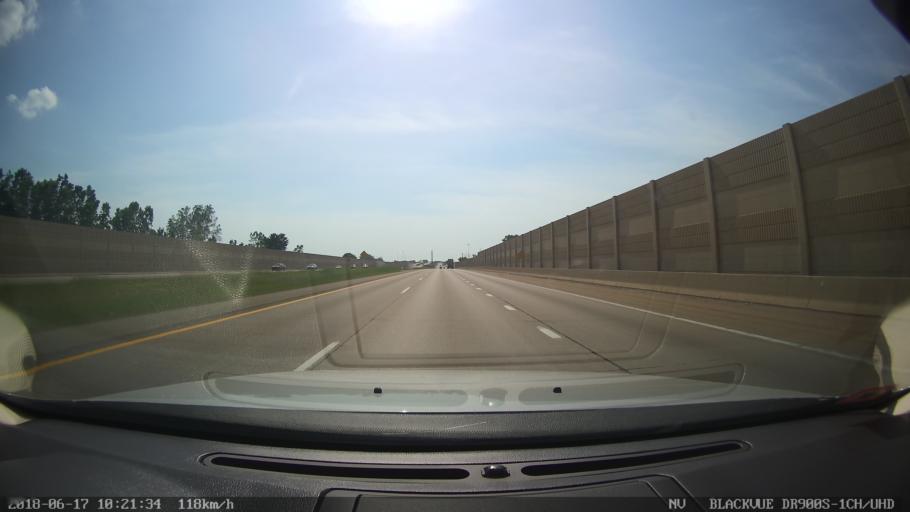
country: US
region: Michigan
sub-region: Kent County
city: Cutlerville
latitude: 42.8490
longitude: -85.6598
